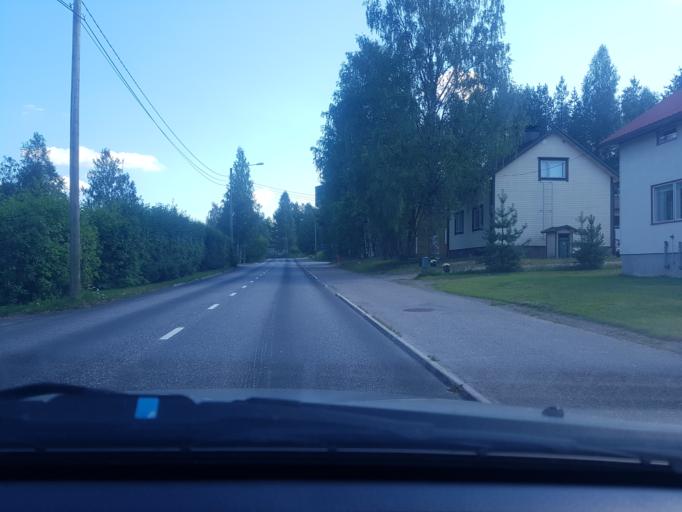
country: FI
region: Kainuu
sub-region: Kehys-Kainuu
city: Kuhmo
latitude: 64.1233
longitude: 29.5166
